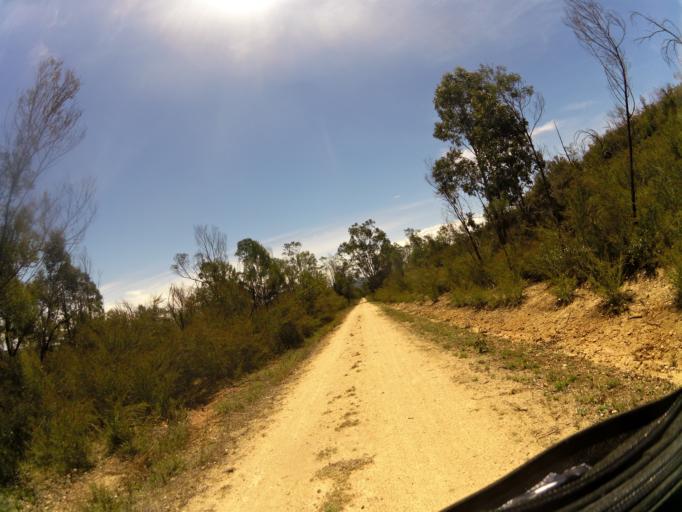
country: AU
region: Victoria
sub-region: East Gippsland
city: Lakes Entrance
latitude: -37.7278
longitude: 147.8524
